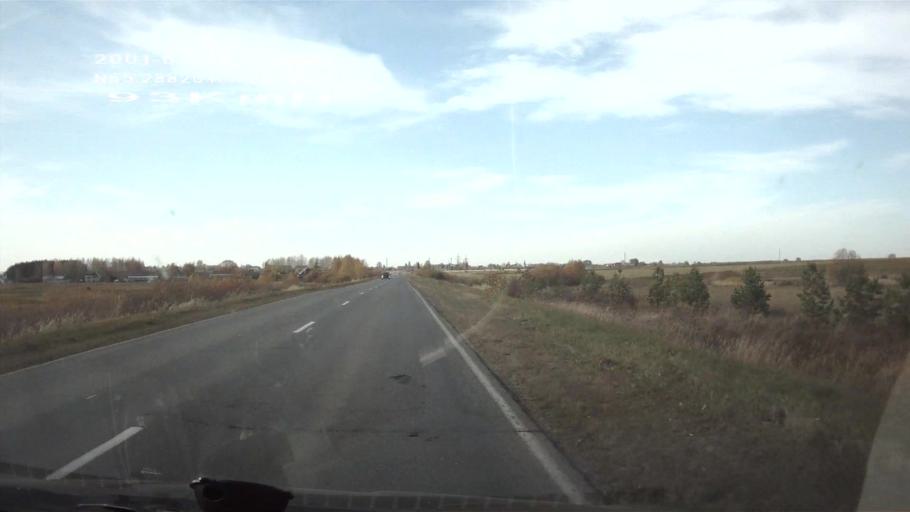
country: RU
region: Chuvashia
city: Ibresi
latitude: 55.2883
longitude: 47.0709
